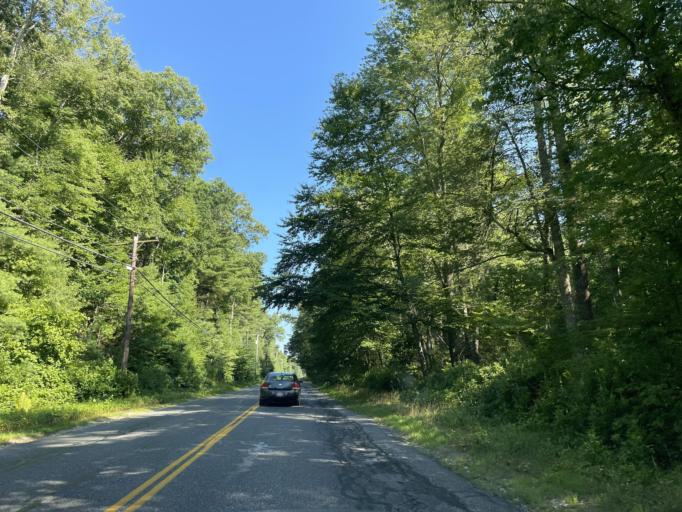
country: US
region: Massachusetts
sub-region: Worcester County
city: East Douglas
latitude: 42.0673
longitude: -71.6970
